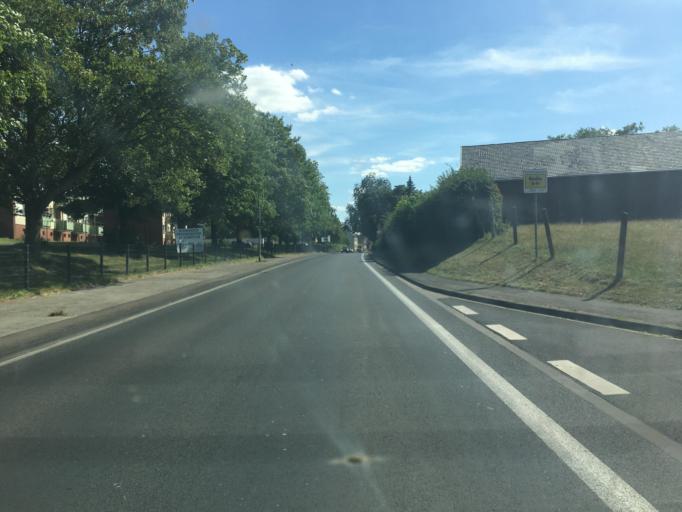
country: DE
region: North Rhine-Westphalia
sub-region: Regierungsbezirk Dusseldorf
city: Rommerskirchen
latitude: 51.0128
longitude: 6.6875
